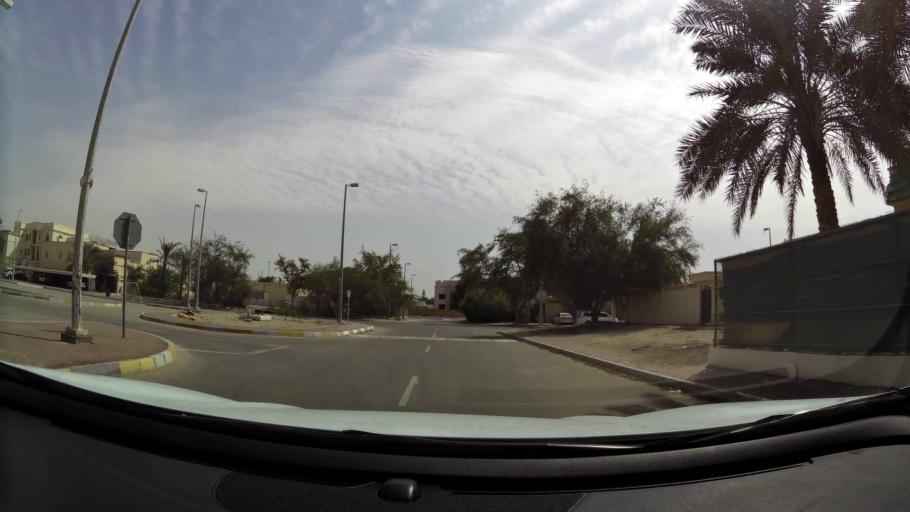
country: AE
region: Abu Dhabi
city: Abu Dhabi
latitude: 24.5490
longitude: 54.6799
